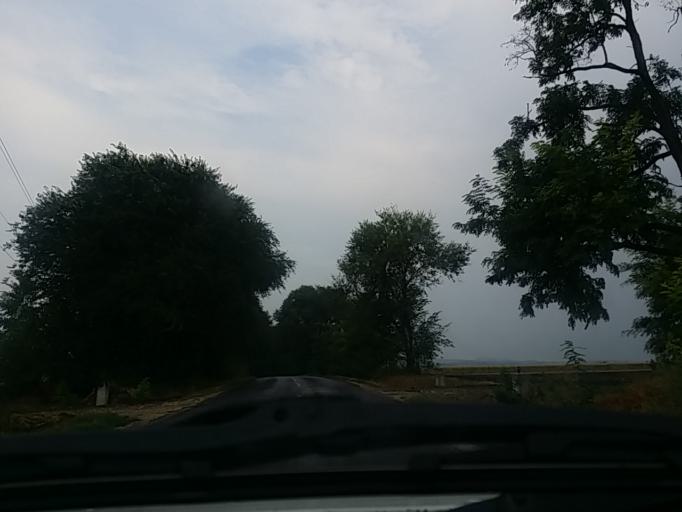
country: HU
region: Pest
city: Paty
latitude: 47.5228
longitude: 18.7996
